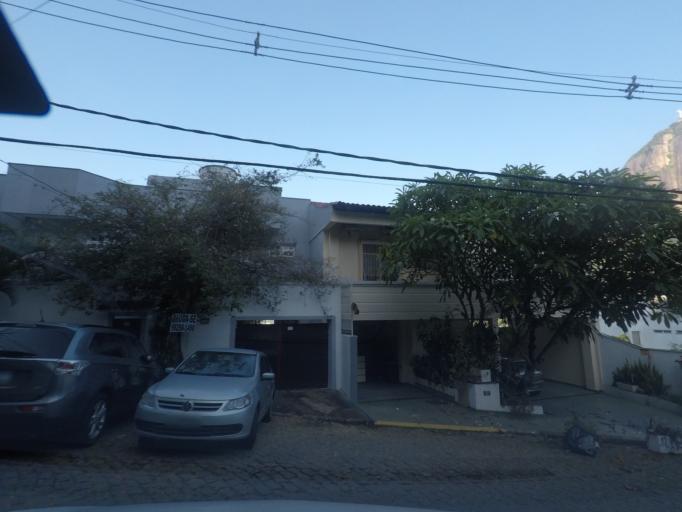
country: BR
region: Rio de Janeiro
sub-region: Rio De Janeiro
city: Rio de Janeiro
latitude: -22.9617
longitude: -43.2004
